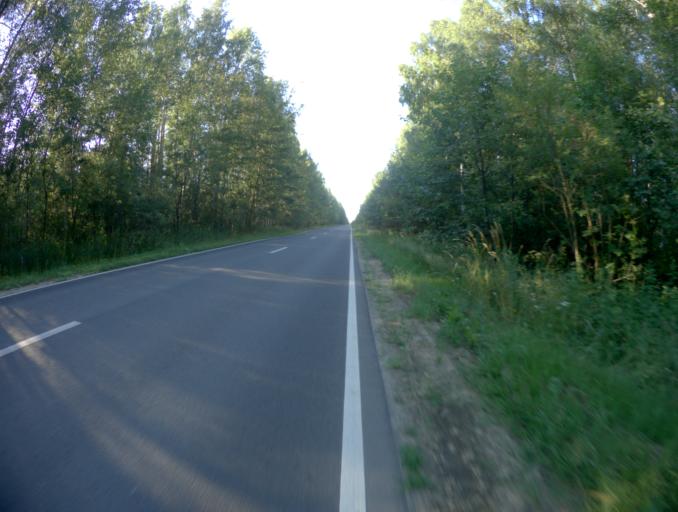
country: RU
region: Vladimir
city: Galitsy
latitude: 56.1078
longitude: 42.8712
